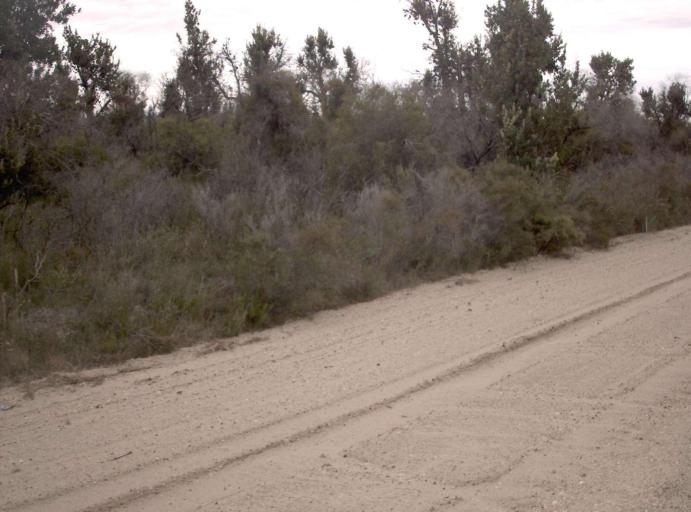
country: AU
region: Victoria
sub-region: East Gippsland
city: Bairnsdale
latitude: -38.1143
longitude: 147.4644
